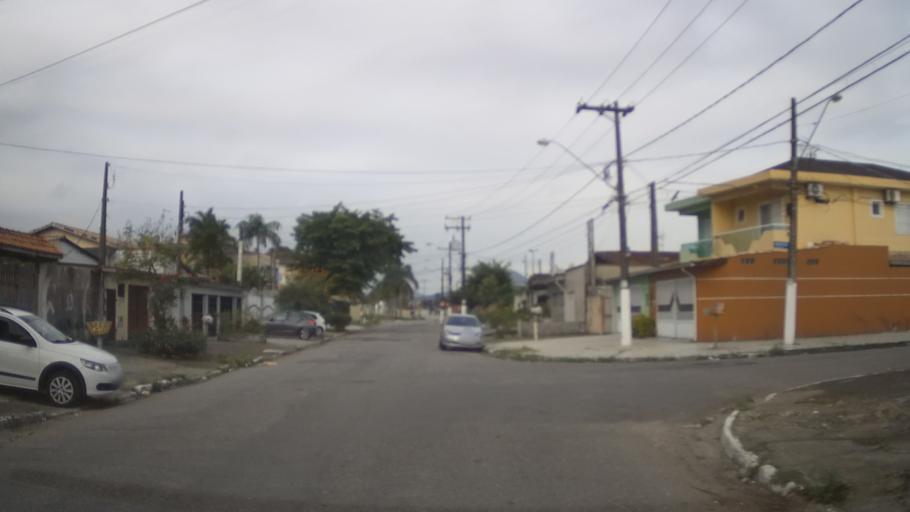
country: BR
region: Sao Paulo
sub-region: Praia Grande
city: Praia Grande
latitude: -24.0107
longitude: -46.4476
